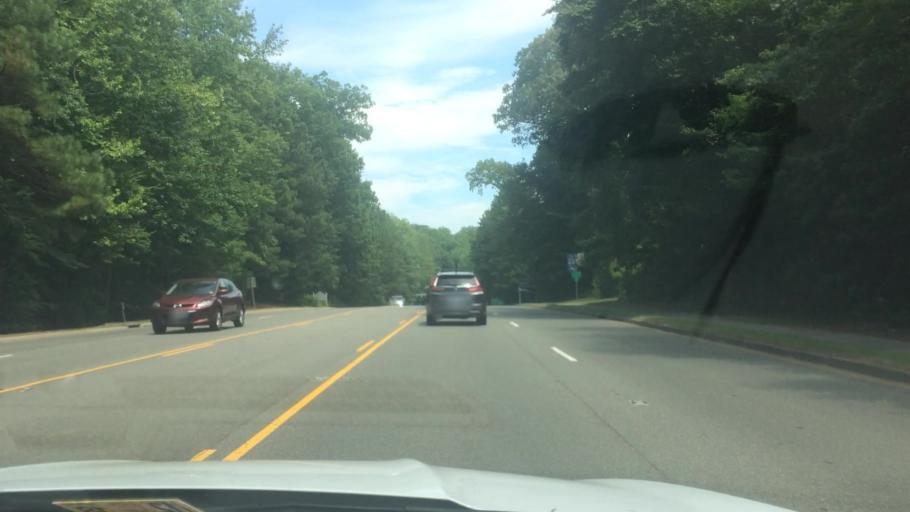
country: US
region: Virginia
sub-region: City of Williamsburg
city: Williamsburg
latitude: 37.2843
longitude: -76.7043
